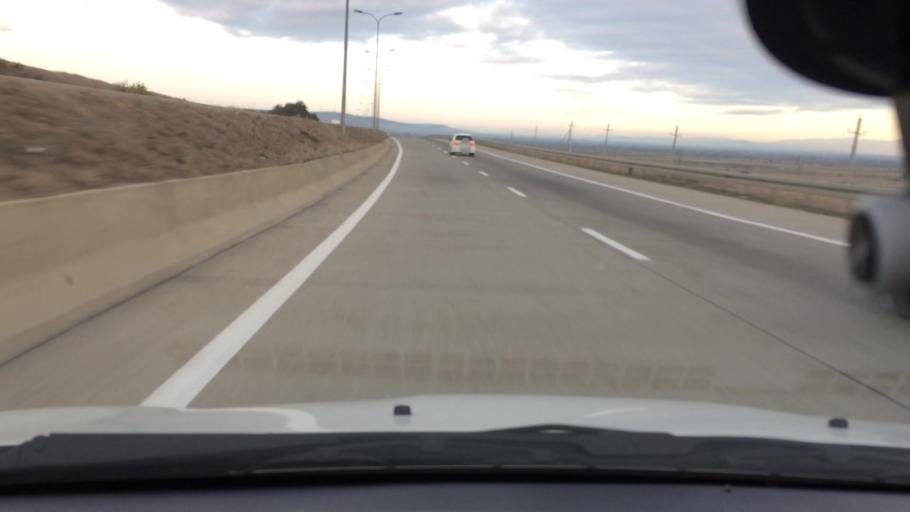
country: GE
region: Shida Kartli
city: Gori
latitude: 42.0276
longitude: 44.2052
